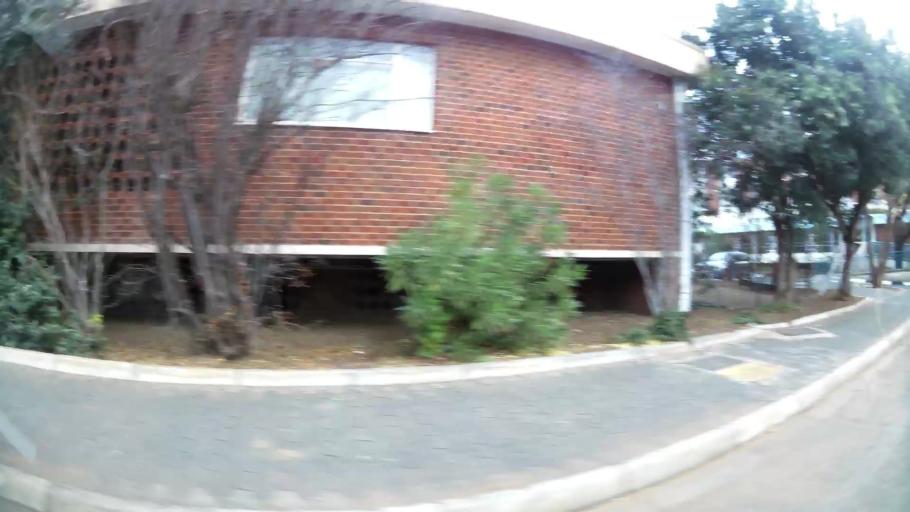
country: ZA
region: Orange Free State
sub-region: Mangaung Metropolitan Municipality
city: Bloemfontein
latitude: -29.1091
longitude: 26.1910
